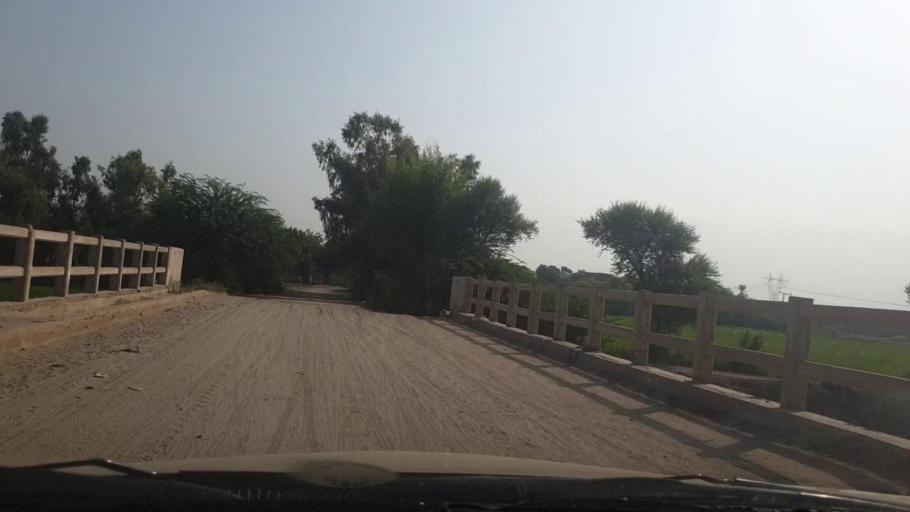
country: PK
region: Sindh
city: Larkana
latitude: 27.5795
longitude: 68.1810
